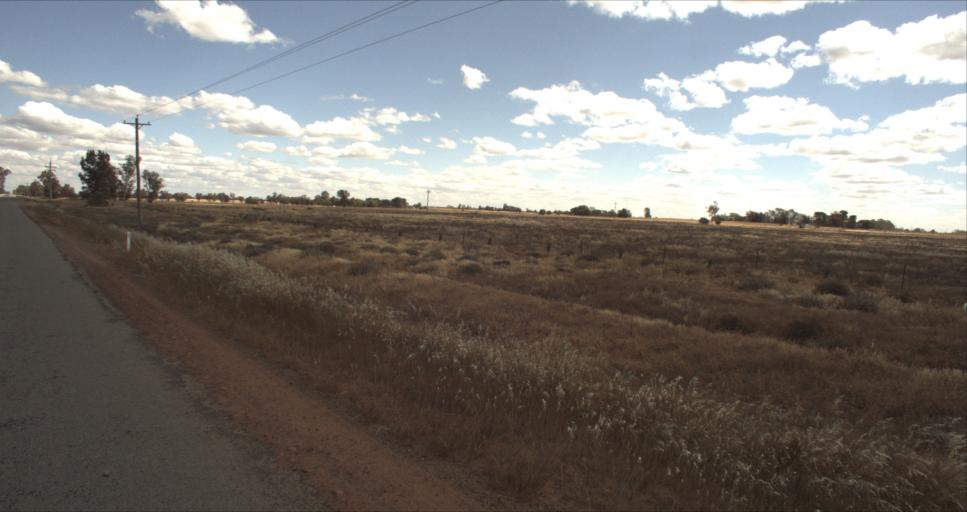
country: AU
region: New South Wales
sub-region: Leeton
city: Leeton
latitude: -34.4810
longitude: 146.2491
